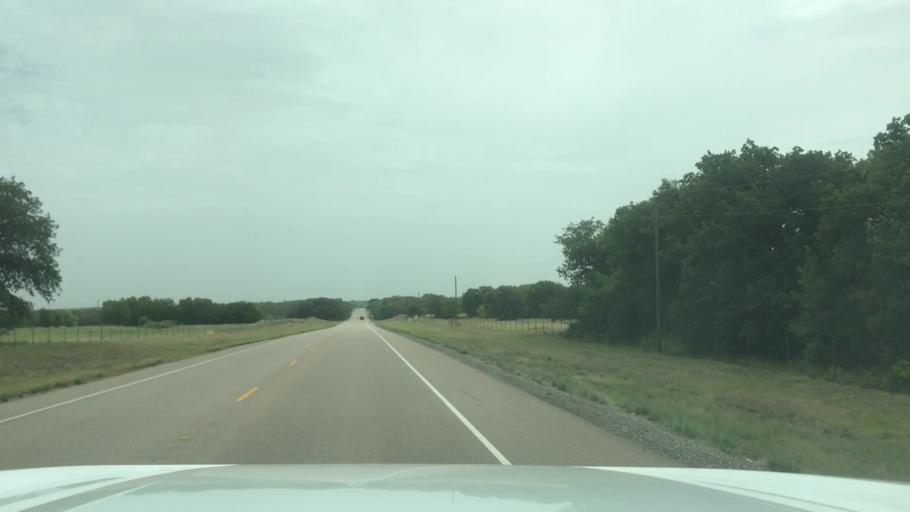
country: US
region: Texas
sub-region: Hamilton County
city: Hico
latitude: 31.9778
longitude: -97.9039
